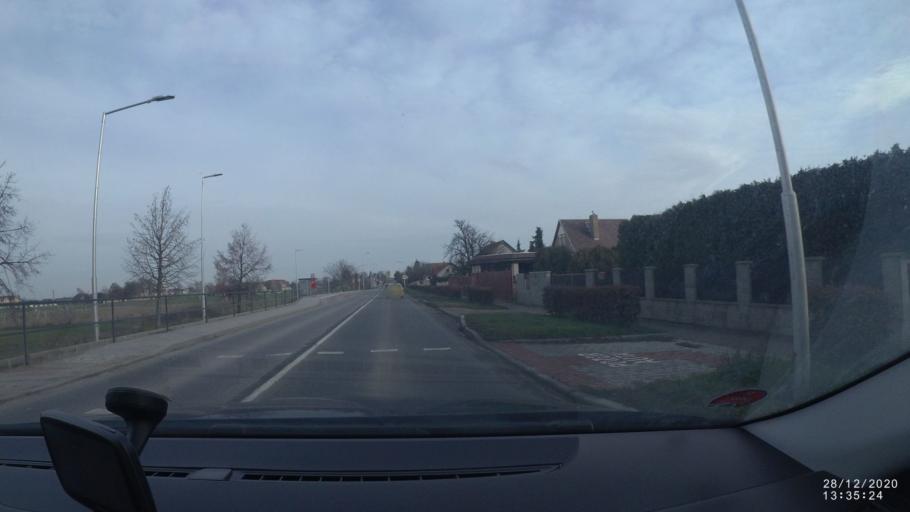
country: CZ
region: Central Bohemia
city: Nehvizdy
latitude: 50.1294
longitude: 14.7191
